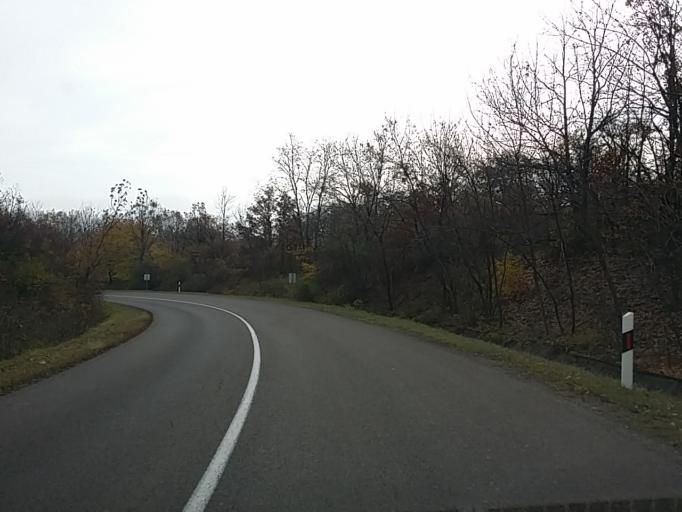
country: HU
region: Heves
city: Gyongyossolymos
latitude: 47.8388
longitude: 19.9562
